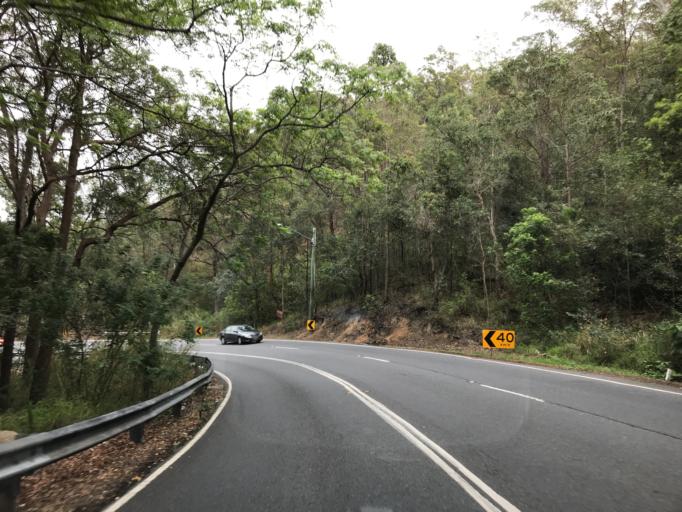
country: AU
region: Queensland
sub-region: Moreton Bay
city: Ferny Hills
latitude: -27.4275
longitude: 152.9437
